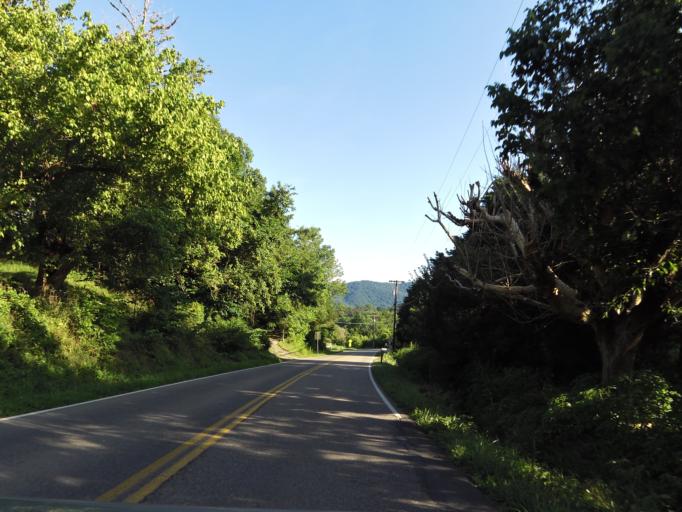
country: US
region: Tennessee
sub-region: Blount County
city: Maryville
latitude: 35.6612
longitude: -83.9618
